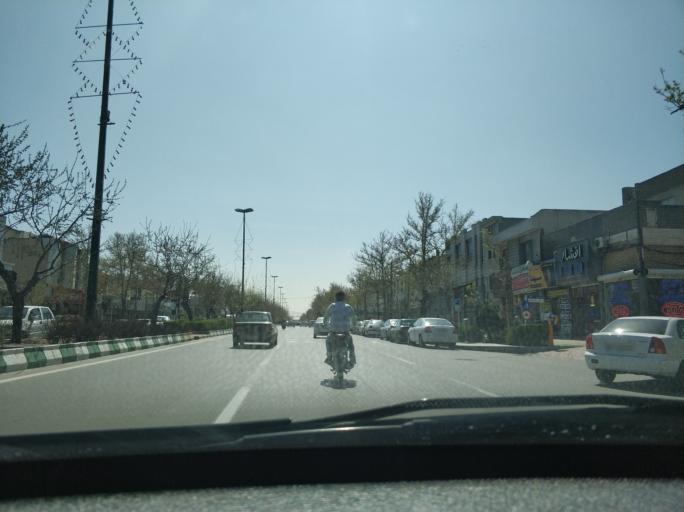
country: IR
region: Razavi Khorasan
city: Mashhad
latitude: 36.2658
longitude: 59.6009
